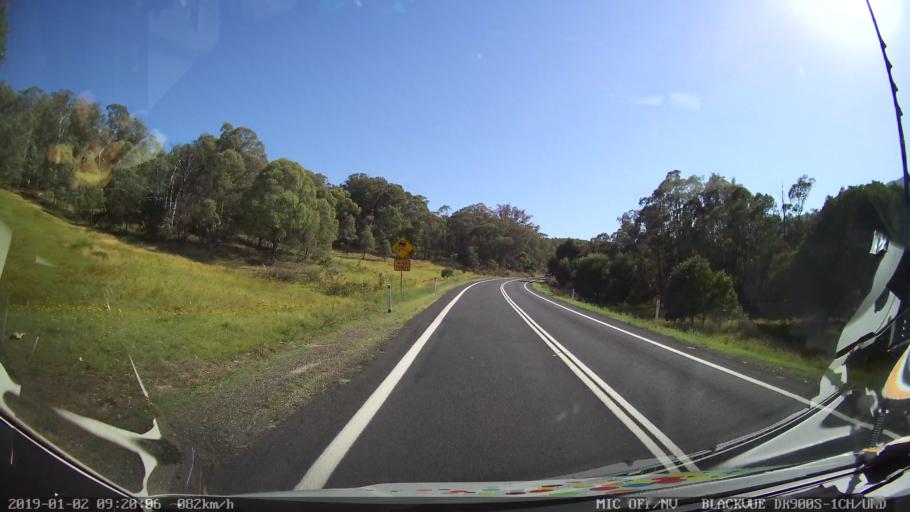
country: AU
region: New South Wales
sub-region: Tumut Shire
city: Tumut
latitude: -35.4154
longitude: 148.2805
